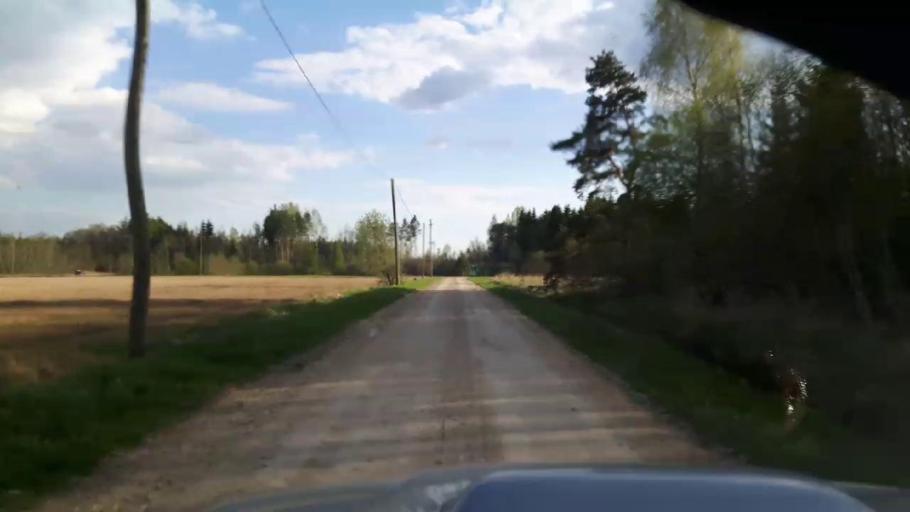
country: EE
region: Paernumaa
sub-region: Sindi linn
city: Sindi
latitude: 58.4319
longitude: 24.8056
